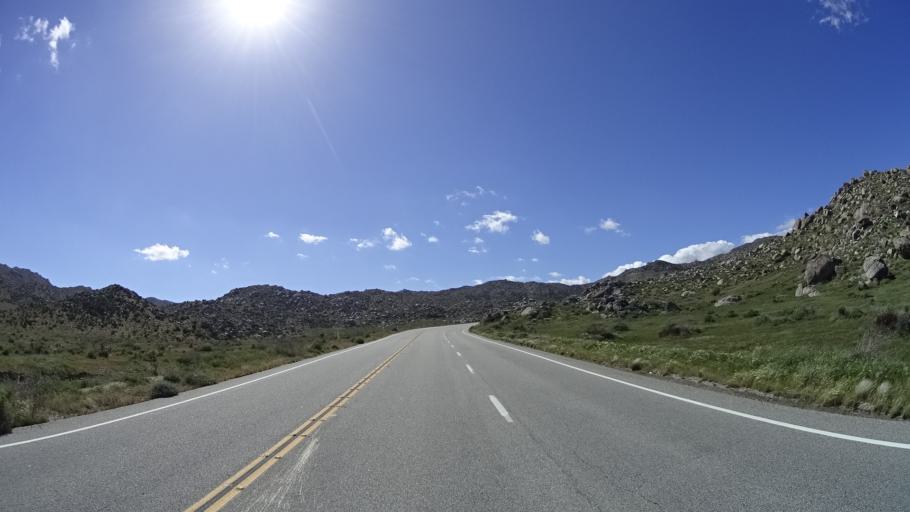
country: US
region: California
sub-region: San Diego County
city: Borrego Springs
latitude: 33.2100
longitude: -116.4501
